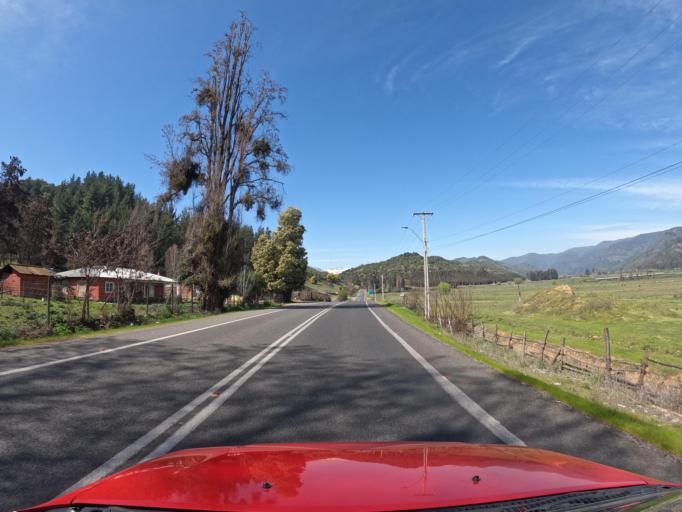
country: CL
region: Maule
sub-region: Provincia de Curico
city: Teno
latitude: -34.9778
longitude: -70.9752
